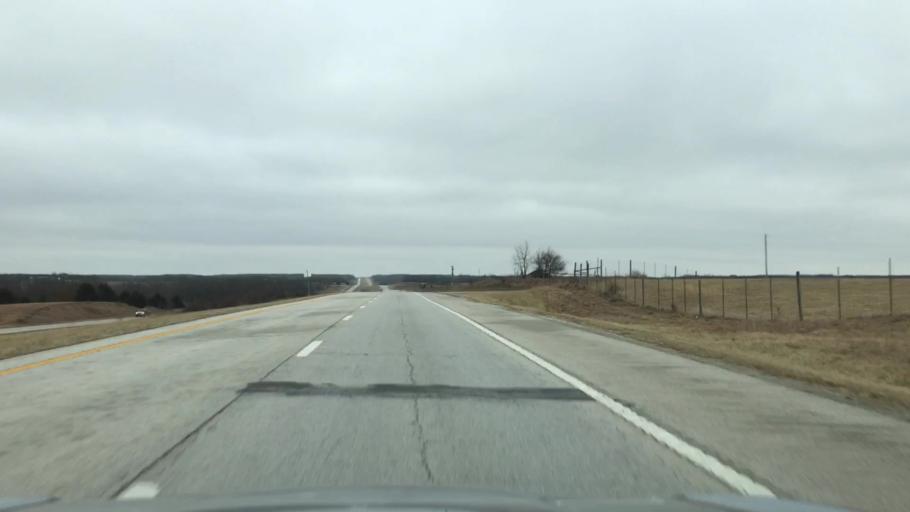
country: US
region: Missouri
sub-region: Linn County
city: Marceline
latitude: 39.7593
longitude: -92.8862
